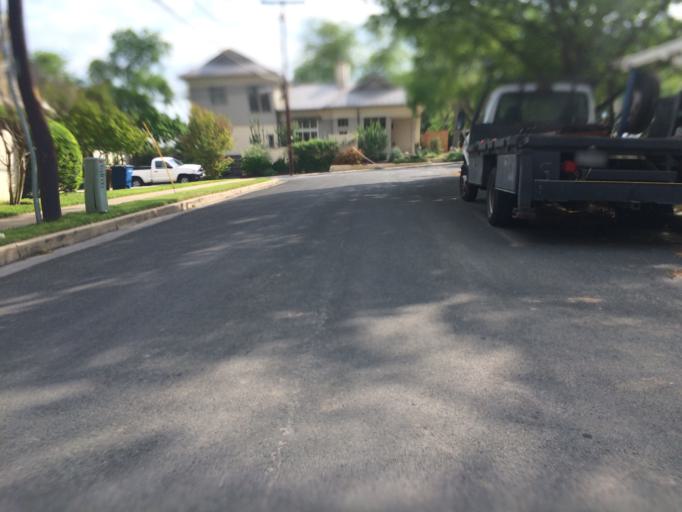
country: US
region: Texas
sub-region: Travis County
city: Austin
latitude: 30.2991
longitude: -97.7426
